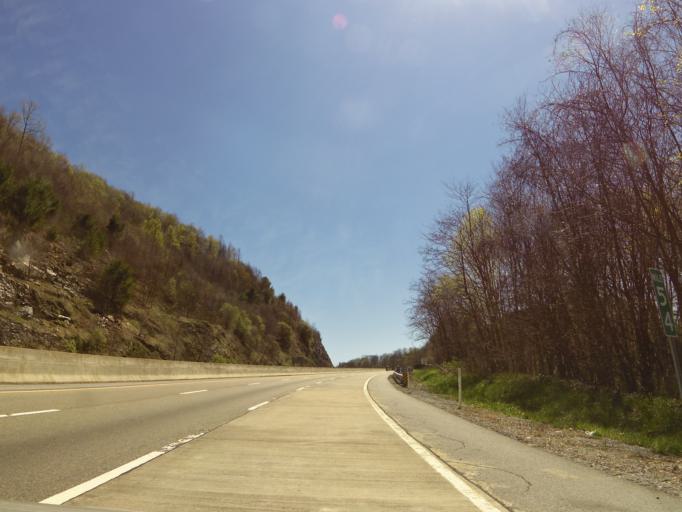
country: US
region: North Carolina
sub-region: Madison County
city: Mars Hill
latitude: 35.9605
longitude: -82.5558
